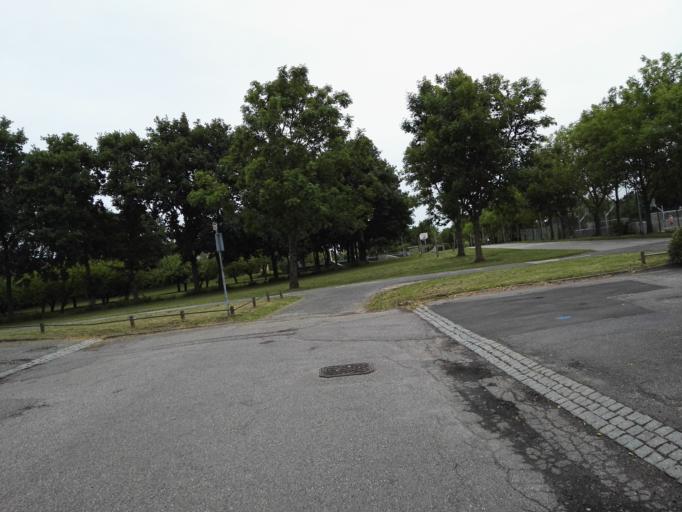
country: DK
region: Zealand
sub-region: Roskilde Kommune
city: Jyllinge
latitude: 55.7477
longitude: 12.1180
